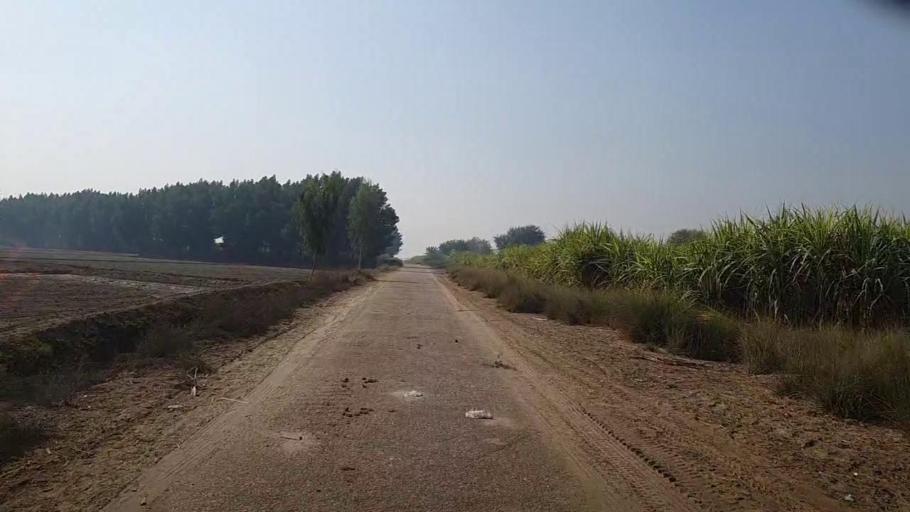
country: PK
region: Sindh
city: Bozdar
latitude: 27.2627
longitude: 68.6209
